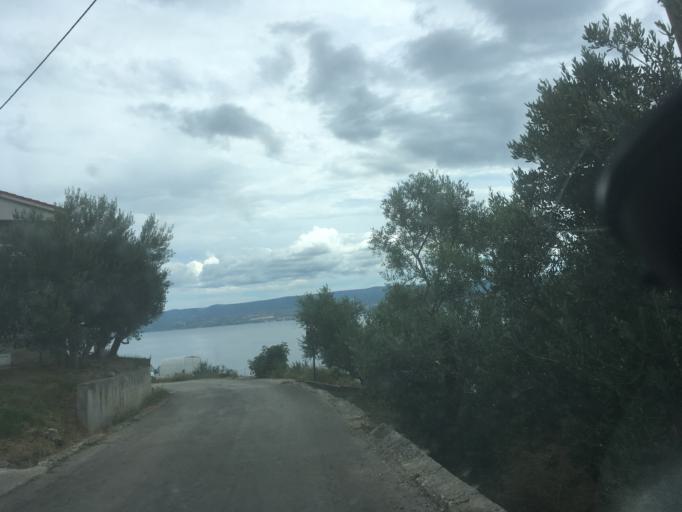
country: HR
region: Splitsko-Dalmatinska
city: Jesenice
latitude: 43.4572
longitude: 16.6207
